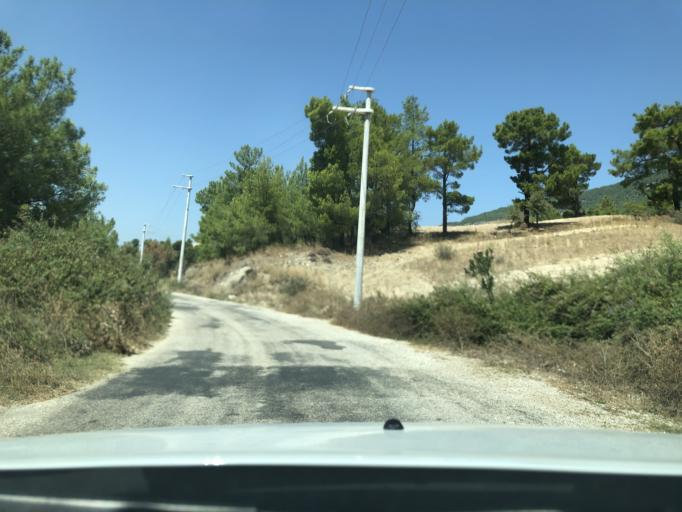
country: TR
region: Antalya
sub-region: Manavgat
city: Kizilagac
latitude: 36.8657
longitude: 31.5589
